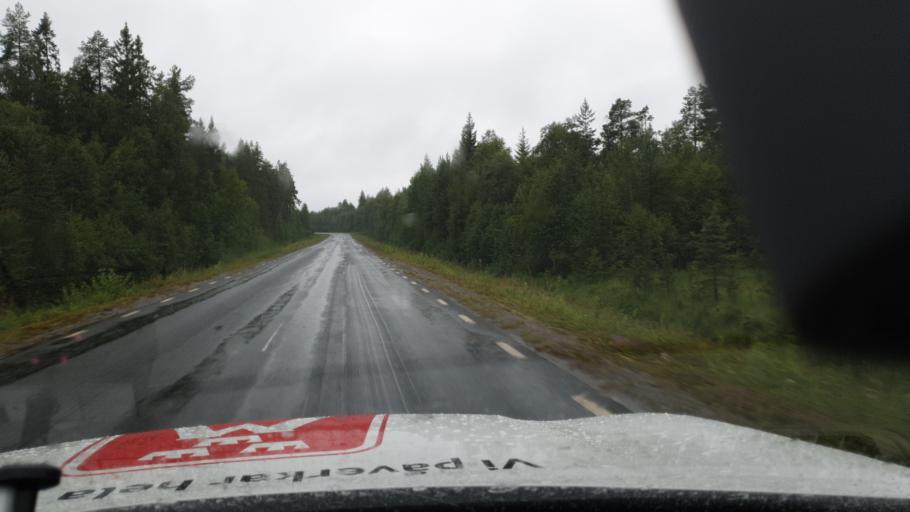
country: SE
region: Vaesterbotten
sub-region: Skelleftea Kommun
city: Soedra Bergsbyn
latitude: 64.5873
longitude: 21.0288
